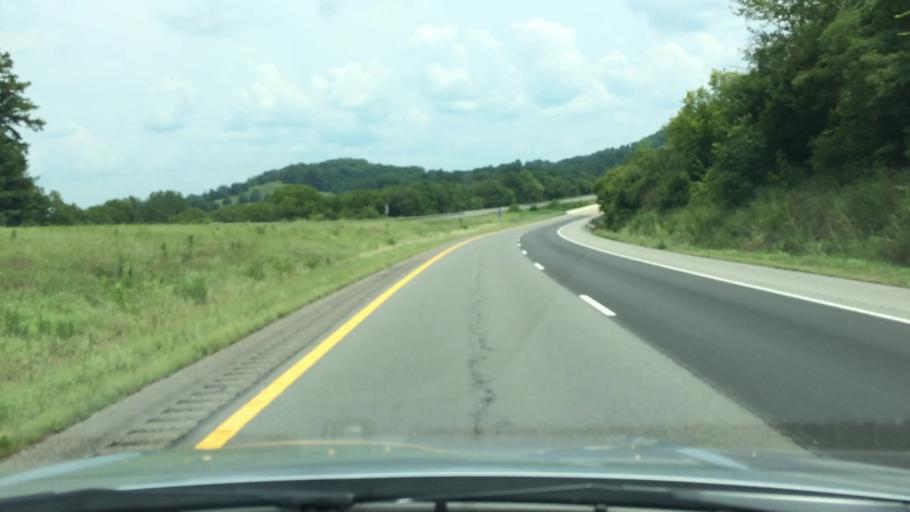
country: US
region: Tennessee
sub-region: Marshall County
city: Cornersville
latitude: 35.2692
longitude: -86.8899
